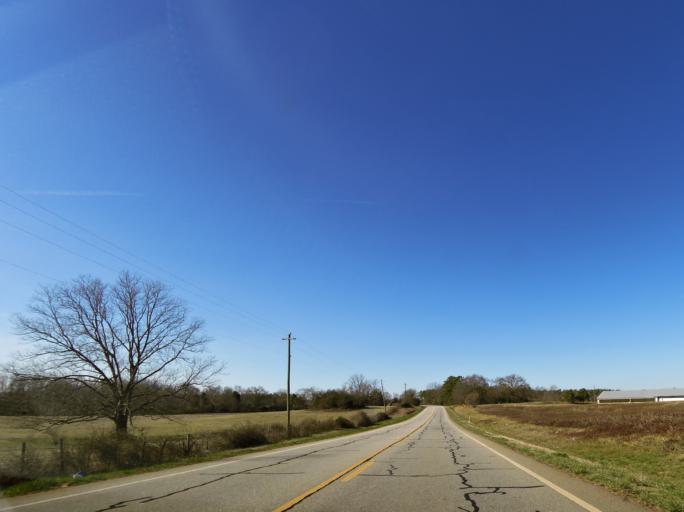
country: US
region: Georgia
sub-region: Lamar County
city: Barnesville
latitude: 32.8873
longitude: -84.1016
